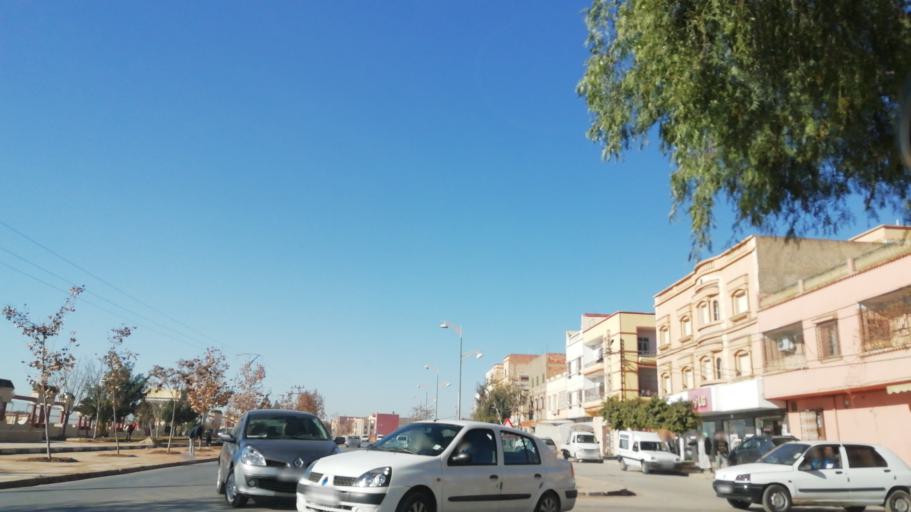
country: DZ
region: Tlemcen
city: Nedroma
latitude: 34.8445
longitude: -1.7543
